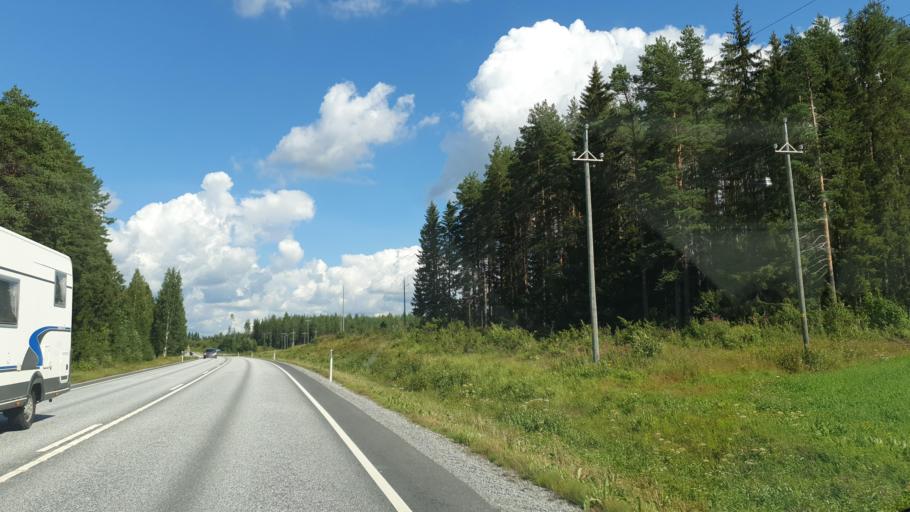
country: FI
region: Northern Savo
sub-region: Ylae-Savo
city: Sonkajaervi
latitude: 63.8459
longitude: 27.4376
